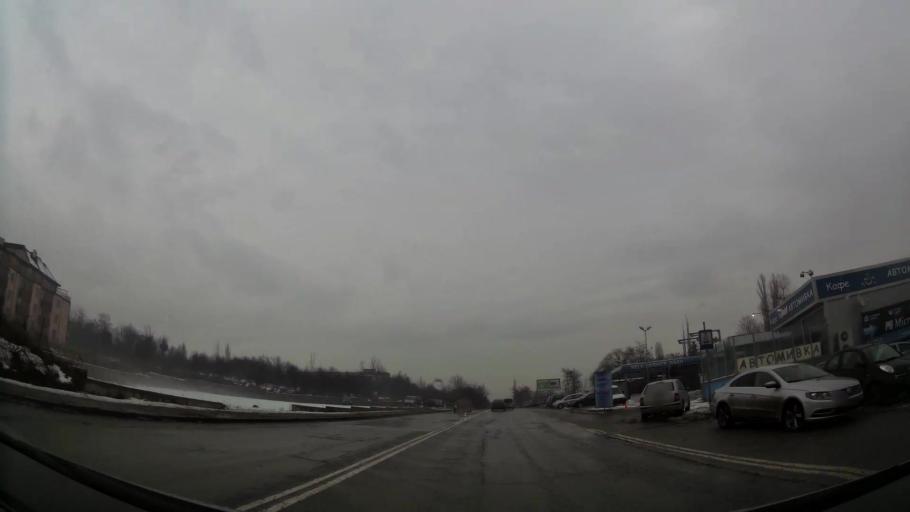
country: BG
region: Sofia-Capital
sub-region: Stolichna Obshtina
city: Sofia
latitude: 42.6743
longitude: 23.2499
